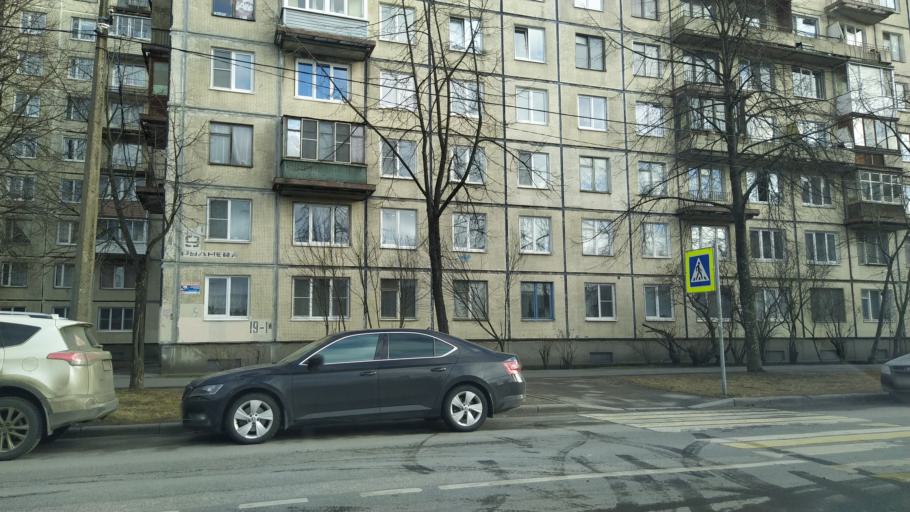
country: RU
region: Leningrad
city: Parnas
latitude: 60.0483
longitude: 30.3678
